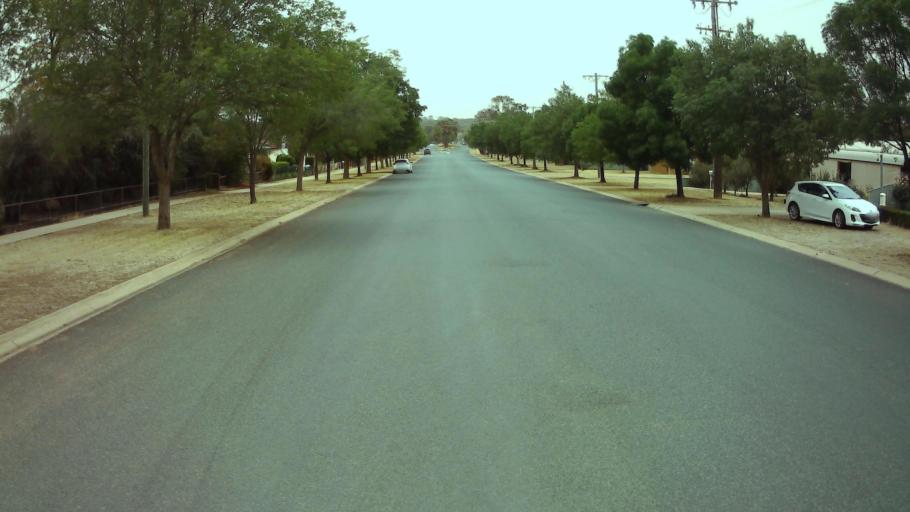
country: AU
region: New South Wales
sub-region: Weddin
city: Grenfell
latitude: -33.8979
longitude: 148.1652
